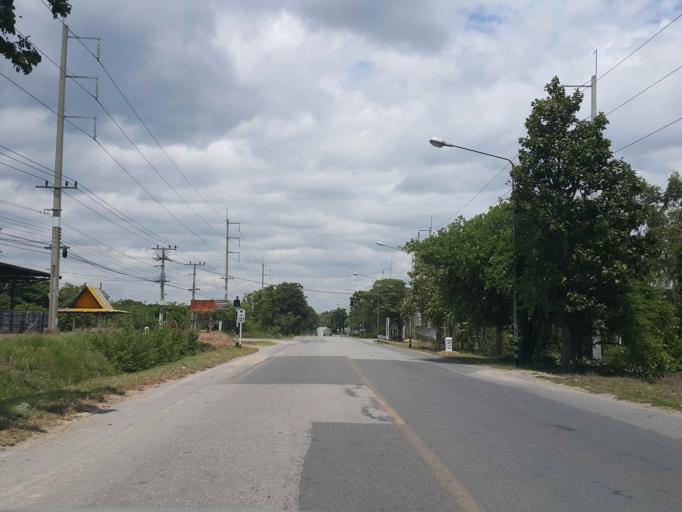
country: TH
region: Lamphun
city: Ban Hong
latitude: 18.3732
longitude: 98.8143
